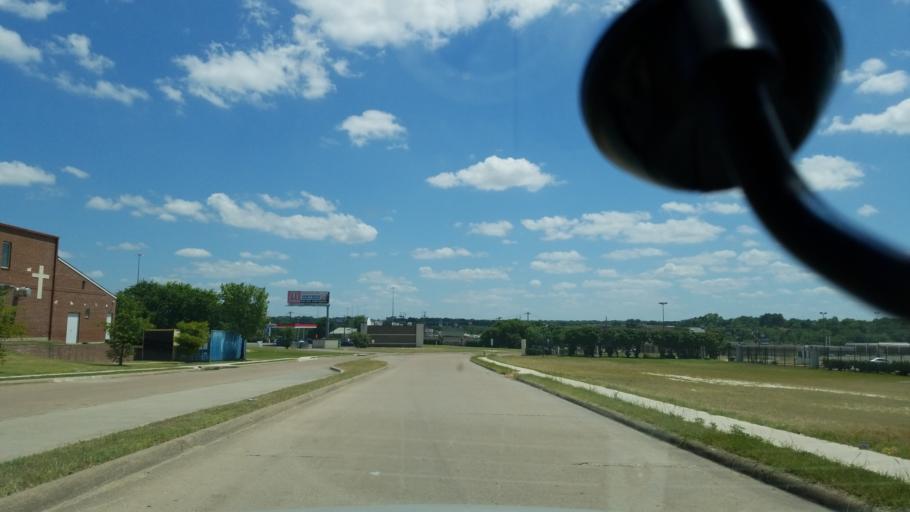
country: US
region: Texas
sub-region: Dallas County
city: Cockrell Hill
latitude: 32.6935
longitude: -96.8245
